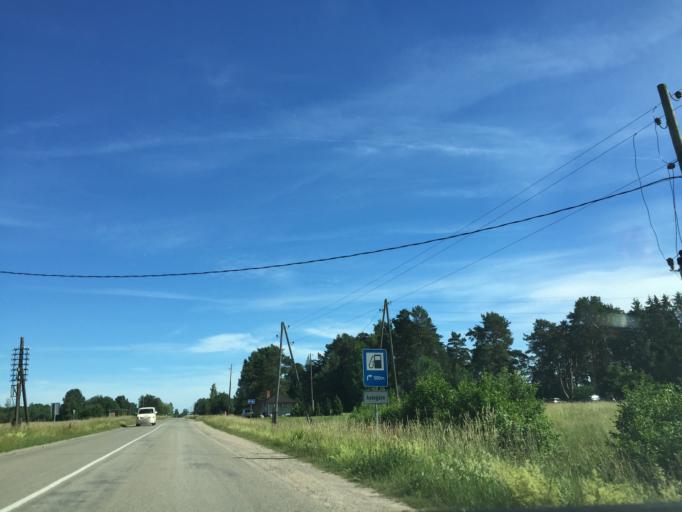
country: LV
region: Rojas
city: Roja
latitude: 57.4533
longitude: 22.8905
